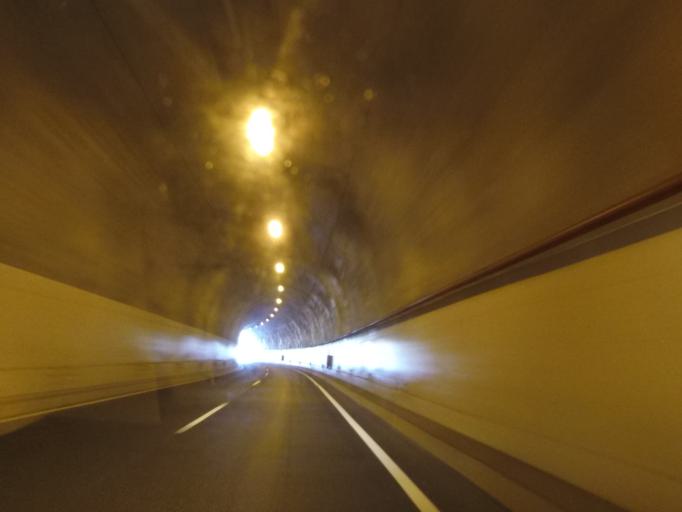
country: PT
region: Madeira
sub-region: Machico
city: Canical
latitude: 32.7415
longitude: -16.7468
